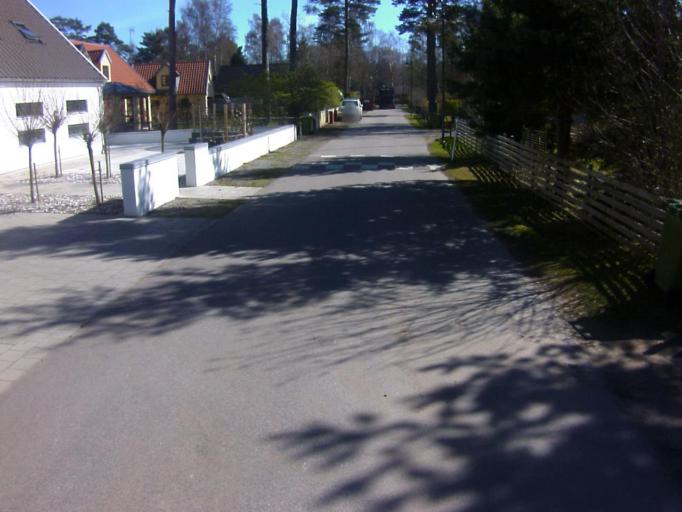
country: SE
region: Skane
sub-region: Kavlinge Kommun
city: Hofterup
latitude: 55.8131
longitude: 12.9781
